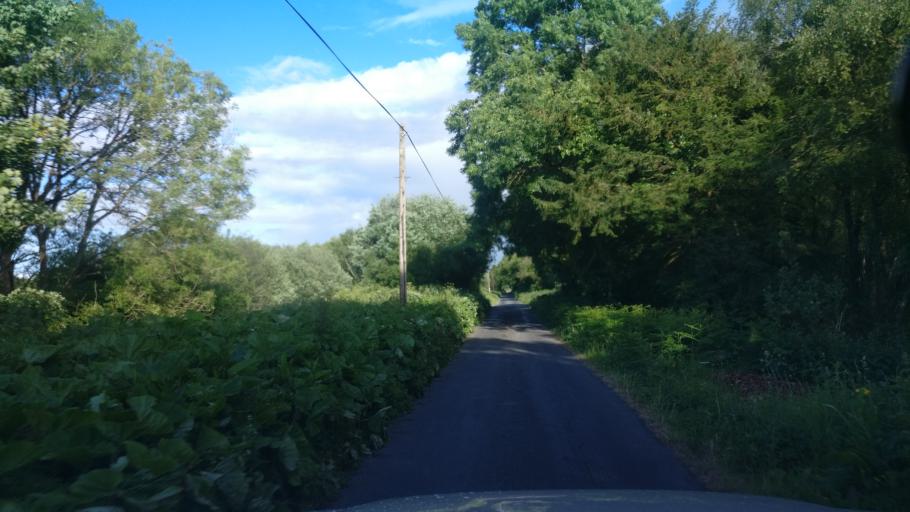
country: IE
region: Connaught
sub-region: County Galway
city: Ballinasloe
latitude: 53.2414
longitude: -8.1919
